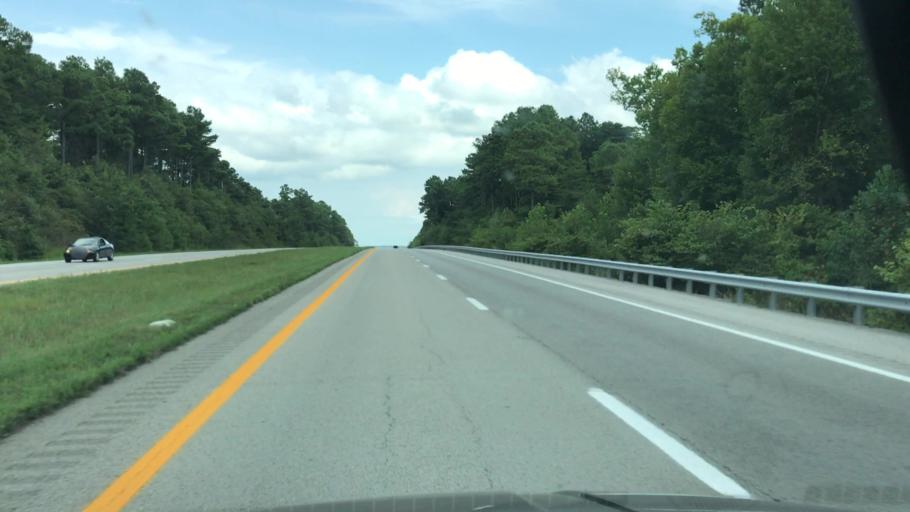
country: US
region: Kentucky
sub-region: Hopkins County
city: Dawson Springs
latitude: 37.1948
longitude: -87.6369
